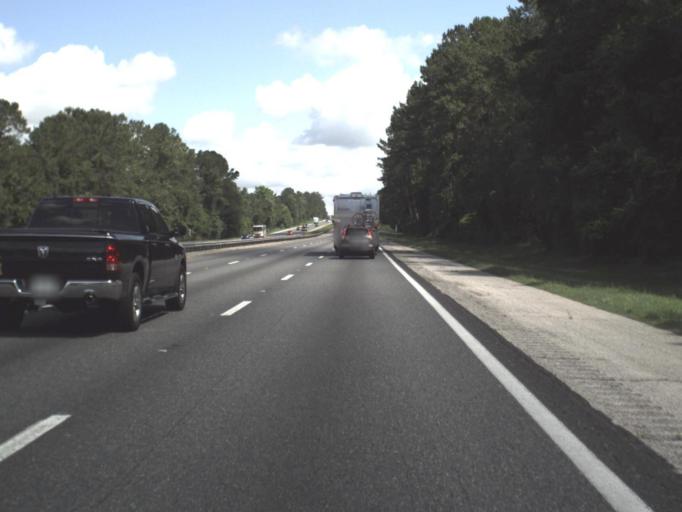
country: US
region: Florida
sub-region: Alachua County
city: Alachua
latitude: 29.7257
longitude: -82.4708
